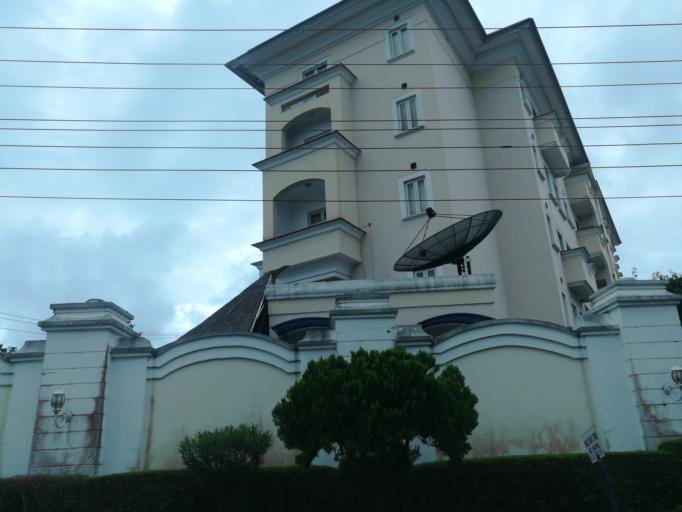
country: NG
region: Lagos
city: Ikoyi
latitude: 6.4478
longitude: 3.4585
